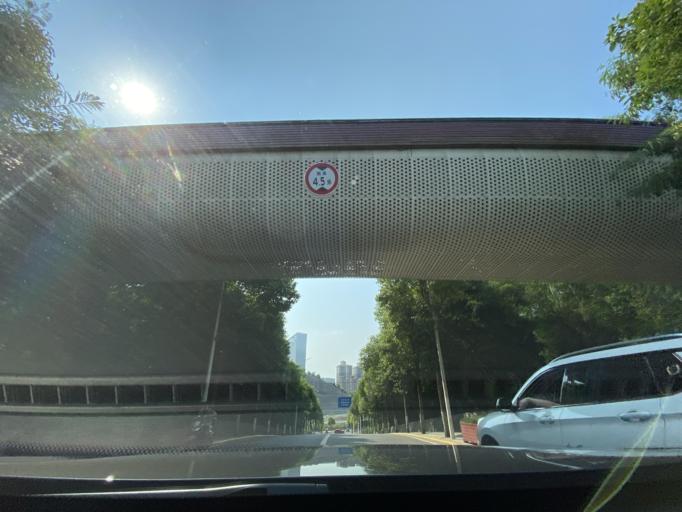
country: CN
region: Sichuan
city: Jiancheng
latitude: 30.4206
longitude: 104.5442
